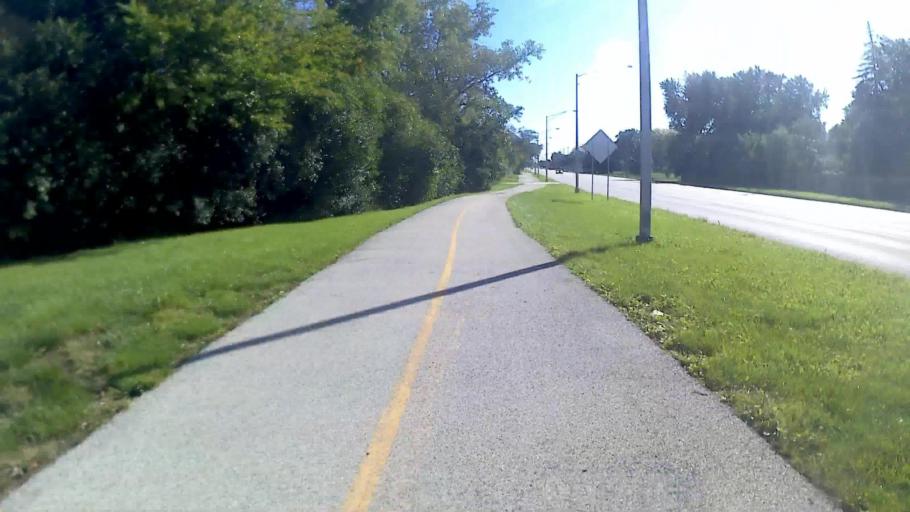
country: US
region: Illinois
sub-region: DuPage County
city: Addison
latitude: 41.9418
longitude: -87.9885
